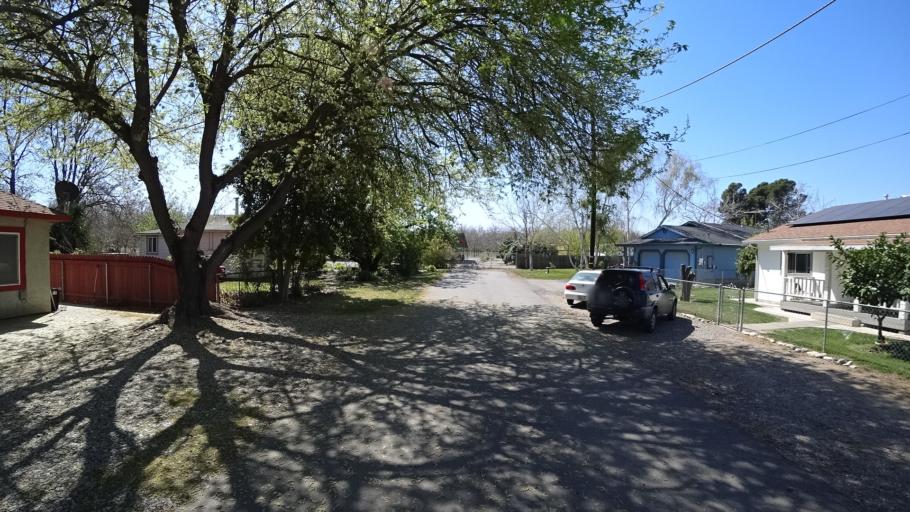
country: US
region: California
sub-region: Glenn County
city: Willows
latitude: 39.4631
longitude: -121.9892
